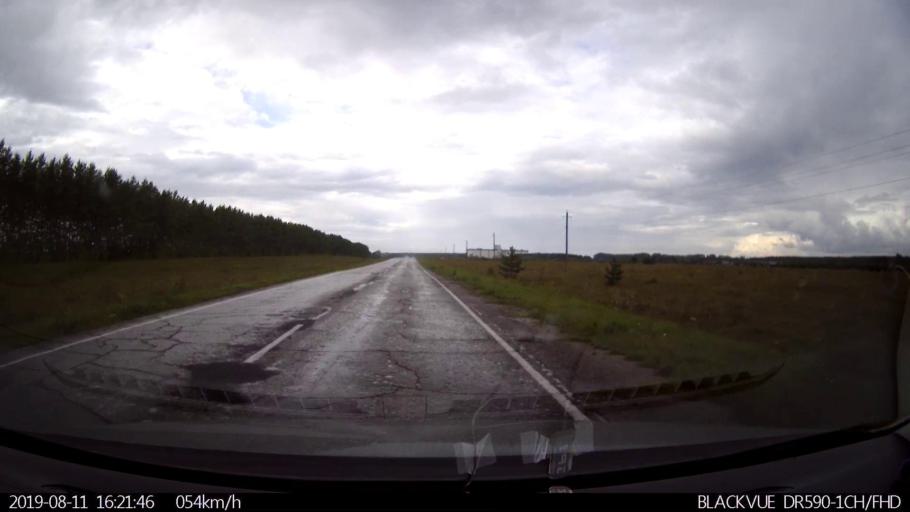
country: RU
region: Ulyanovsk
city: Mayna
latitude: 54.0824
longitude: 47.5964
